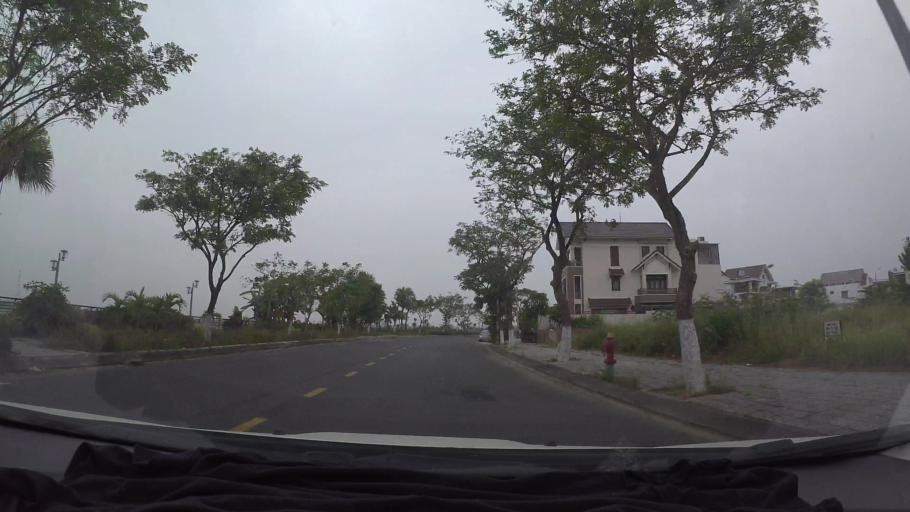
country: VN
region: Da Nang
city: Ngu Hanh Son
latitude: 16.0314
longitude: 108.2332
